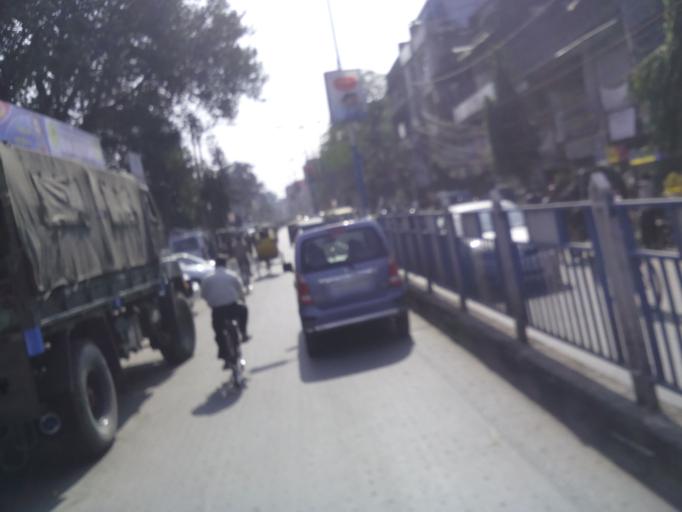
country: IN
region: West Bengal
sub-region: Darjiling
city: Shiliguri
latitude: 26.7142
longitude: 88.4262
